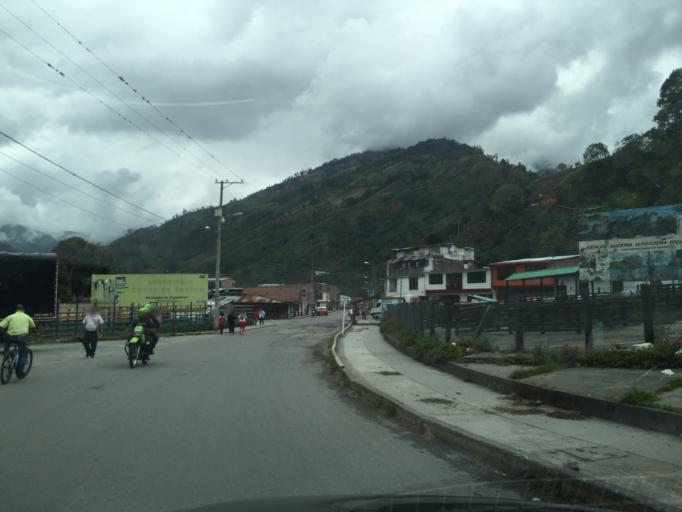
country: CO
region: Tolima
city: Cajamarca
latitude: 4.4396
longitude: -75.4279
